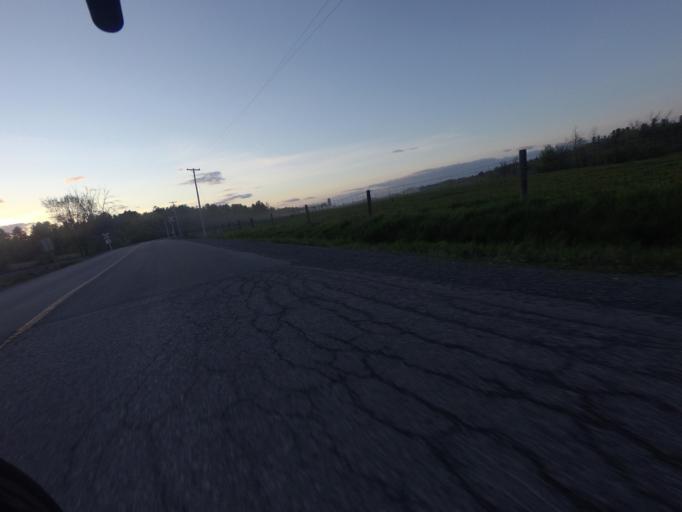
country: CA
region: Ontario
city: Arnprior
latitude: 45.3991
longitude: -76.1981
